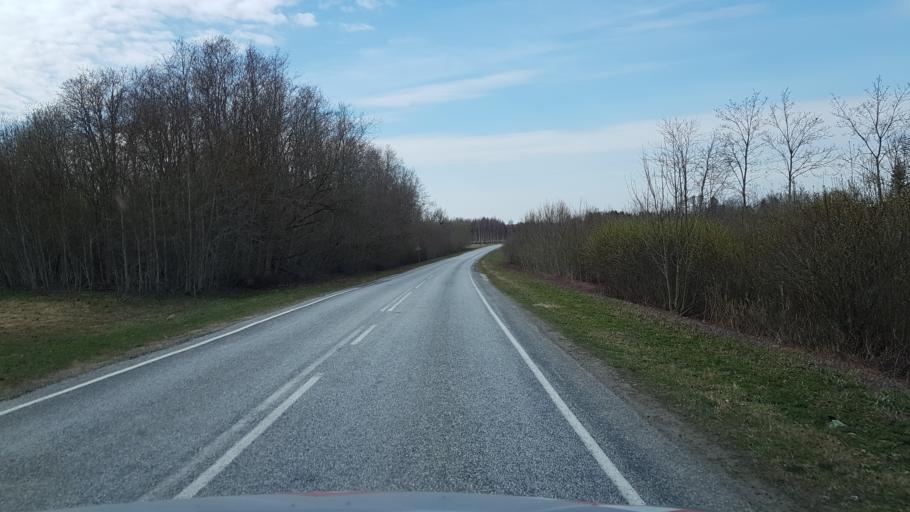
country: EE
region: Laeaene-Virumaa
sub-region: Haljala vald
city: Haljala
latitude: 59.4759
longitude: 26.1616
